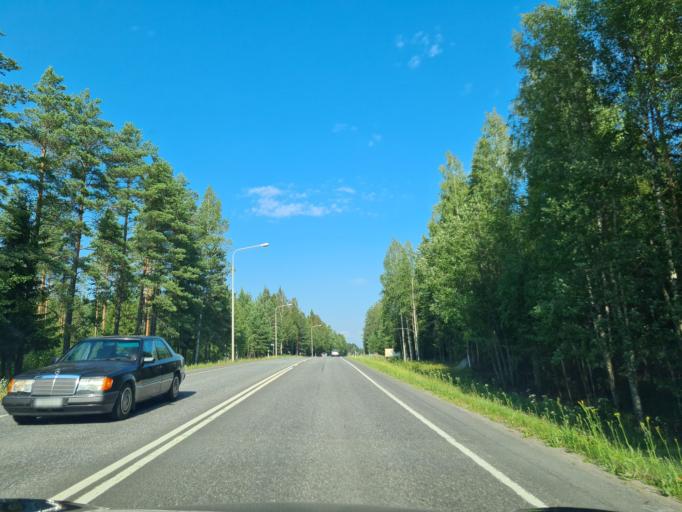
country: FI
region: Satakunta
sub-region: Pohjois-Satakunta
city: Kankaanpaeae
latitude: 61.8325
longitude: 22.4074
